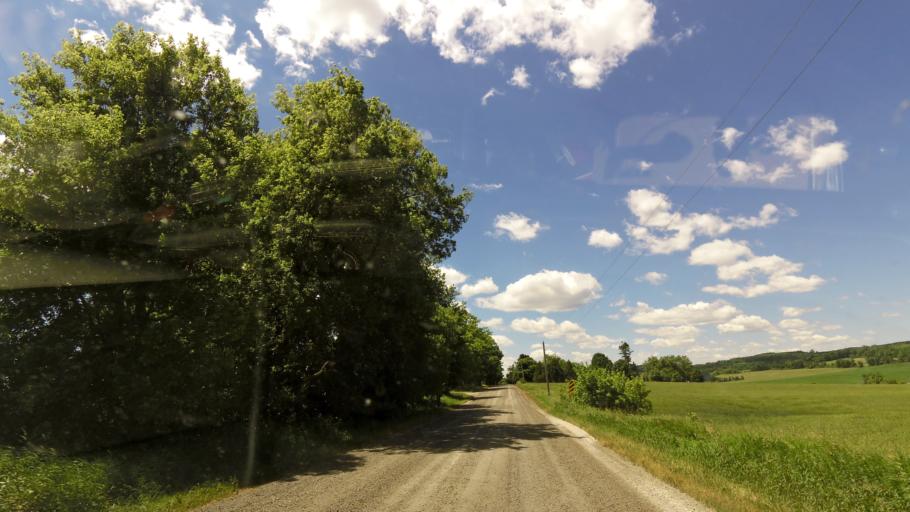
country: CA
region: Ontario
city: Omemee
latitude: 43.9949
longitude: -78.5092
